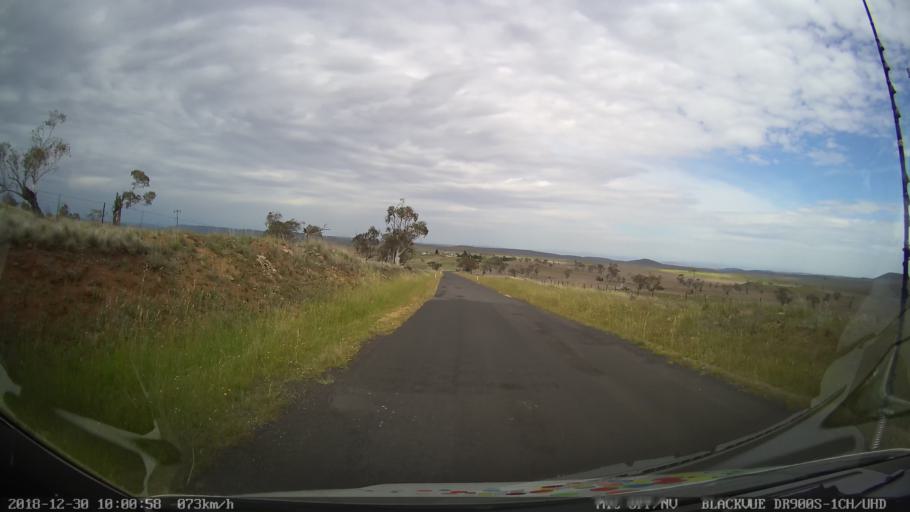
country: AU
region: New South Wales
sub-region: Cooma-Monaro
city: Cooma
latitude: -36.5135
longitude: 149.1930
